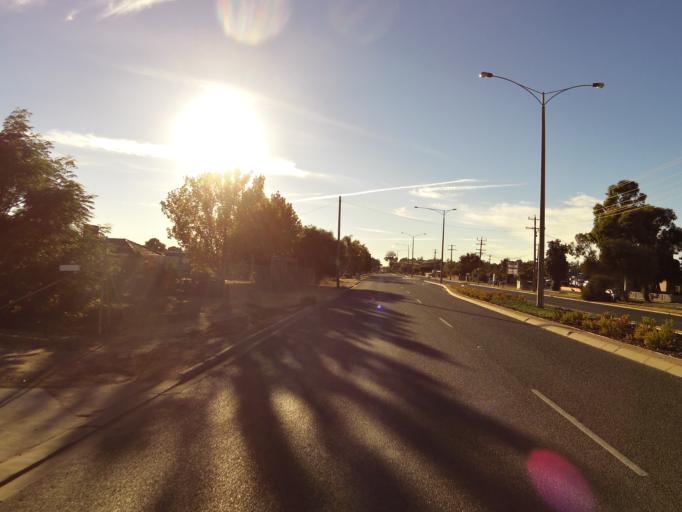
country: AU
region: Victoria
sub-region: Campaspe
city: Echuca
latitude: -36.1404
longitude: 144.7325
